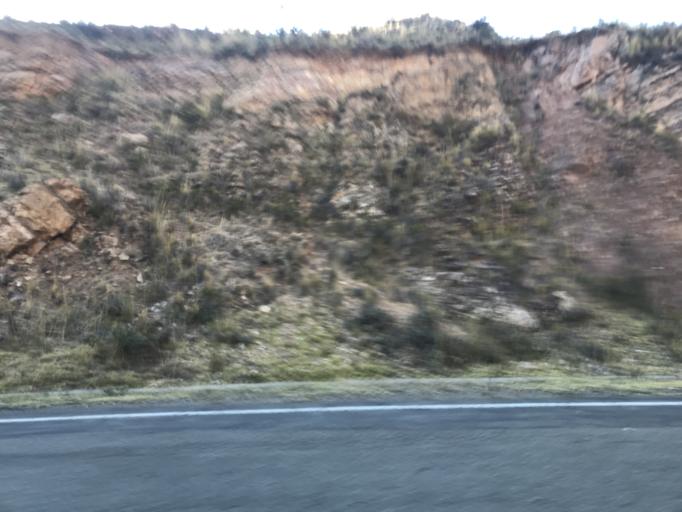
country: BO
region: La Paz
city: San Pedro
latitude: -16.2271
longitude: -68.8513
